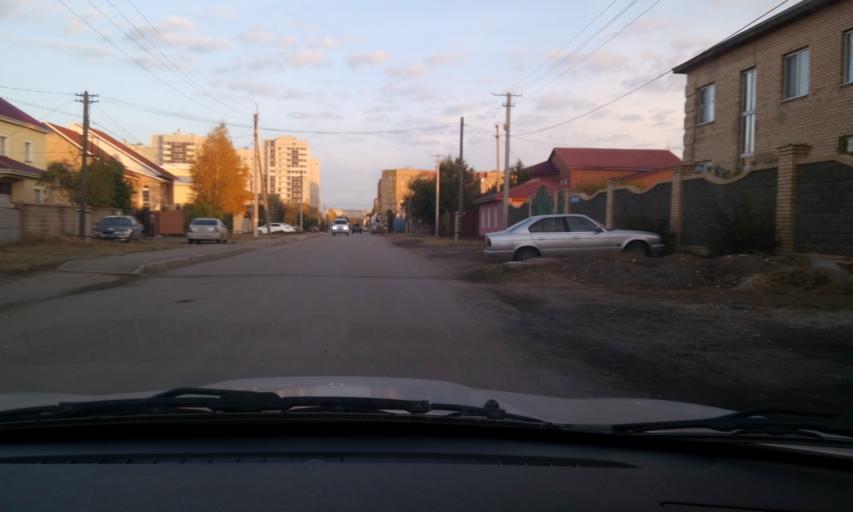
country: KZ
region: Astana Qalasy
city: Astana
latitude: 51.1375
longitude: 71.4877
